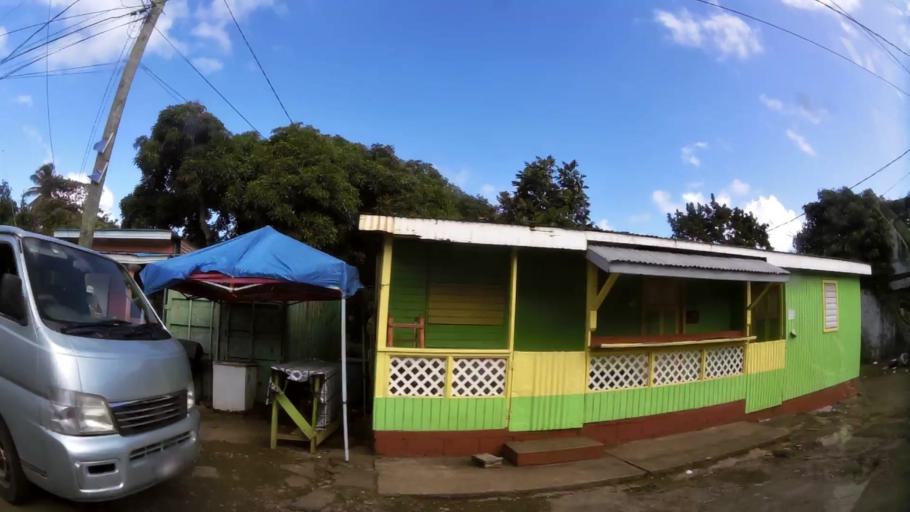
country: DM
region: Saint Andrew
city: Marigot
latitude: 15.5375
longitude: -61.2812
